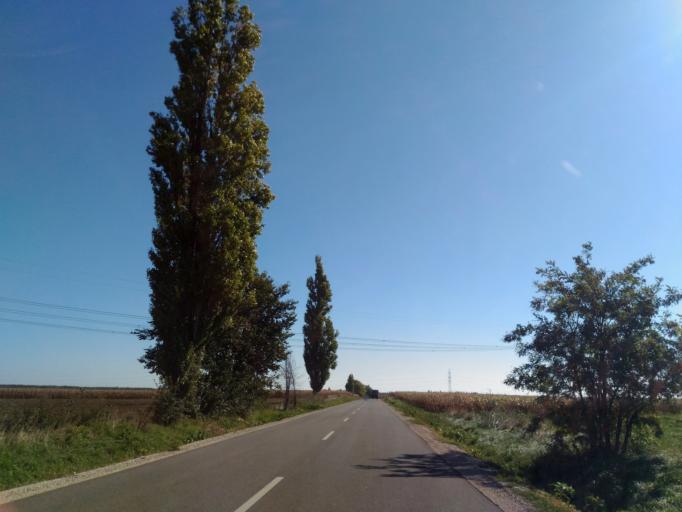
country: HU
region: Fejer
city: Pusztaszabolcs
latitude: 47.1346
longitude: 18.7919
